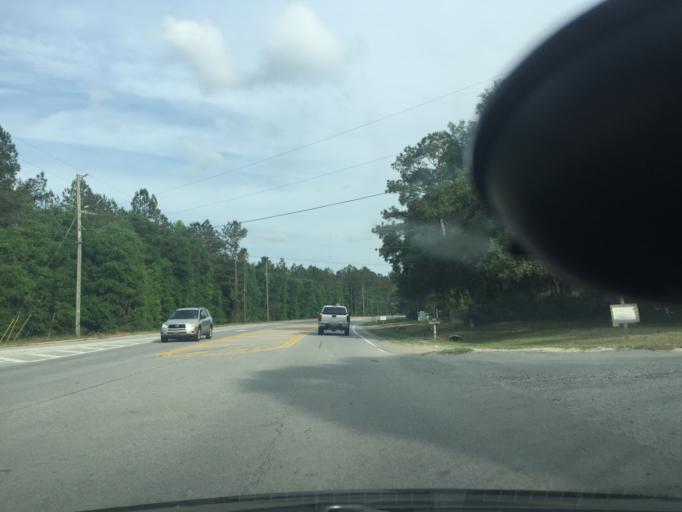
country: US
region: Georgia
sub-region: Chatham County
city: Bloomingdale
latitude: 32.0732
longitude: -81.3623
